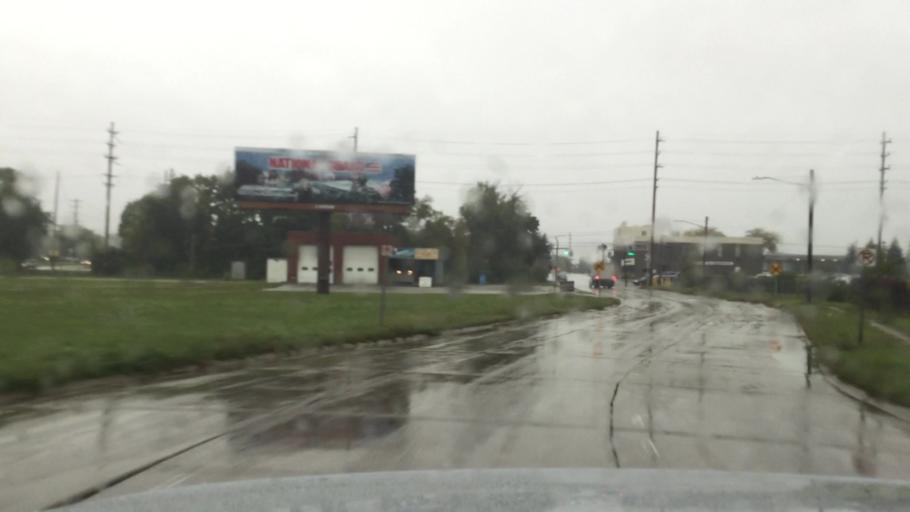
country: US
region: Michigan
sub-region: Saginaw County
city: Saginaw
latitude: 43.4185
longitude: -83.9438
